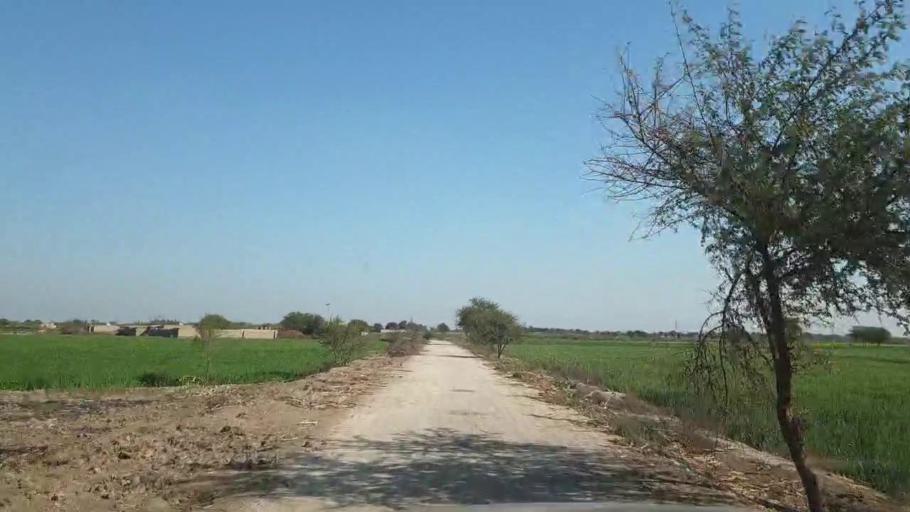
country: PK
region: Sindh
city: Tando Adam
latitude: 25.6651
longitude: 68.6948
